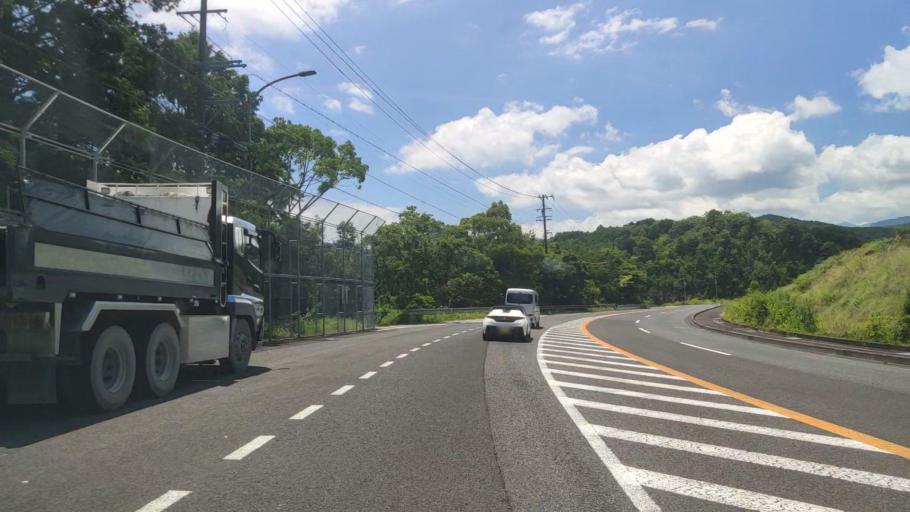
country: JP
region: Mie
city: Owase
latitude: 34.1514
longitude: 136.2567
